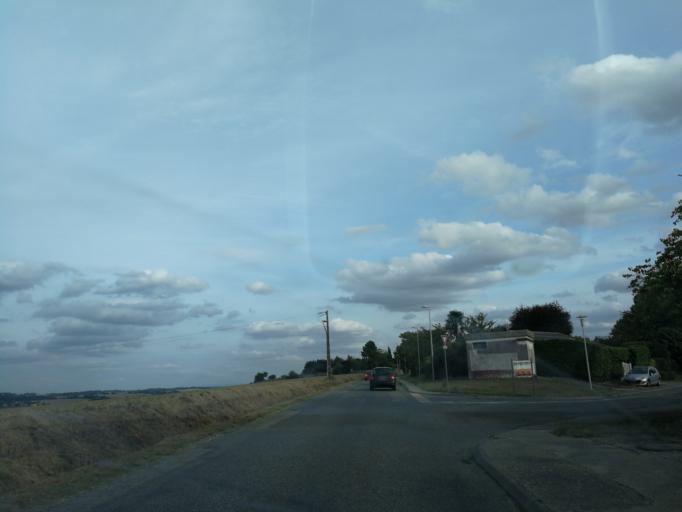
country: FR
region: Midi-Pyrenees
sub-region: Departement de la Haute-Garonne
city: Flourens
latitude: 43.5948
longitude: 1.5703
